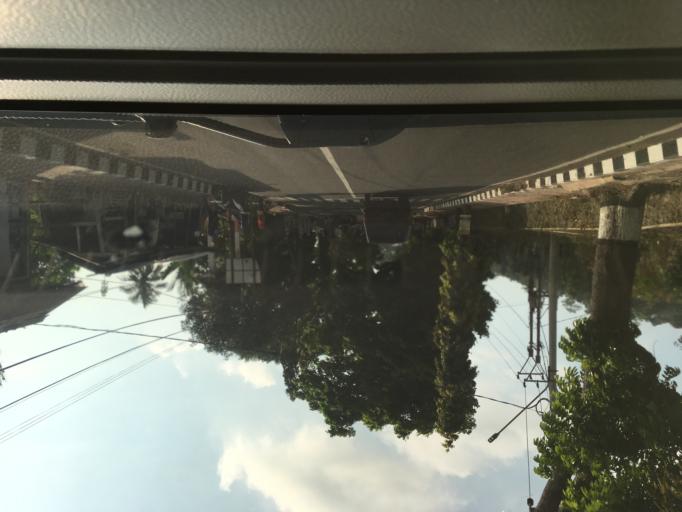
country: ID
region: West Java
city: Kuningan
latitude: -6.9809
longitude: 108.4663
